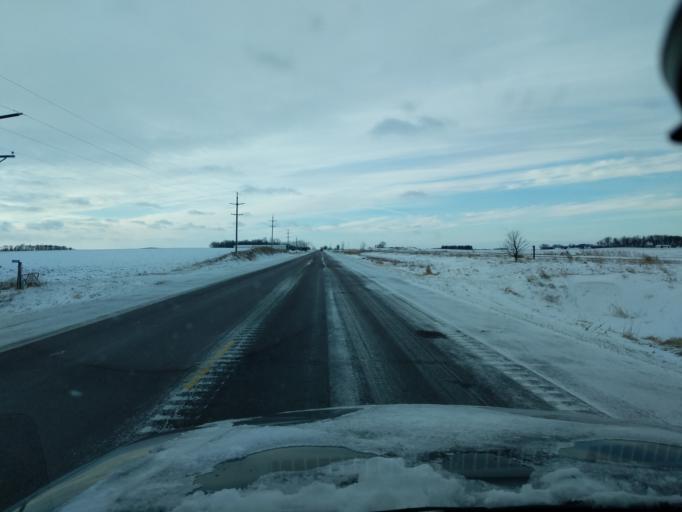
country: US
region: Minnesota
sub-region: Renville County
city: Hector
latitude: 44.7236
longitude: -94.5076
